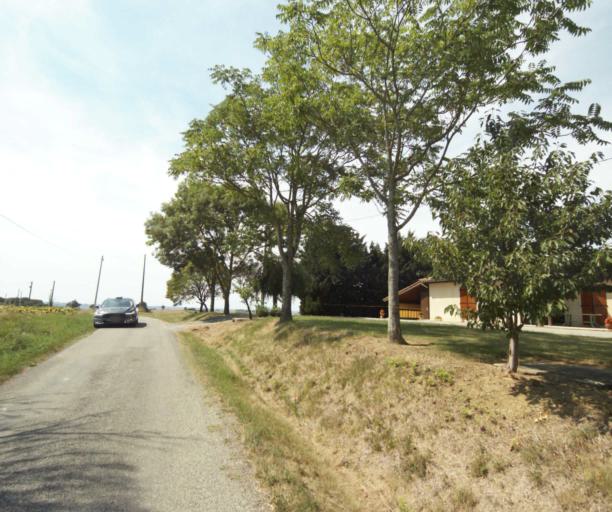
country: FR
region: Midi-Pyrenees
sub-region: Departement de la Haute-Garonne
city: Gaillac-Toulza
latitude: 43.2469
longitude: 1.4203
